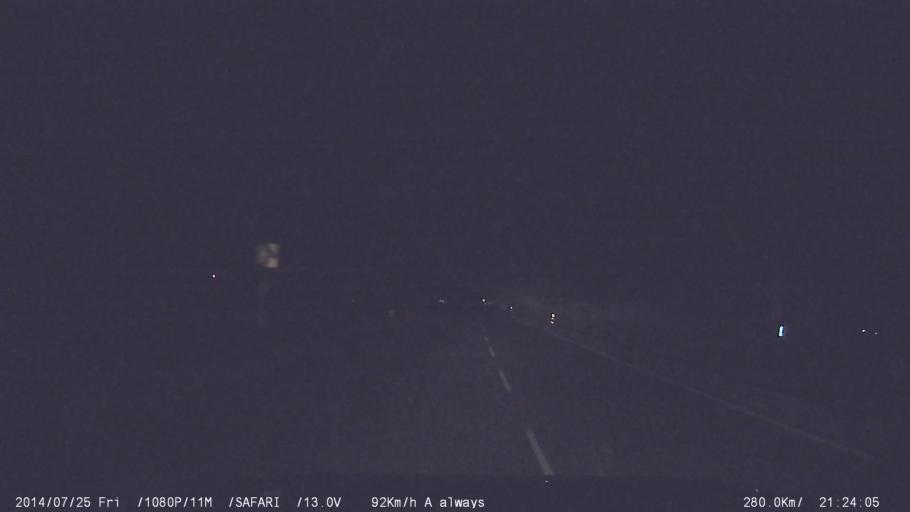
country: IN
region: Tamil Nadu
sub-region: Erode
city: Perundurai
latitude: 11.2644
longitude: 77.5529
